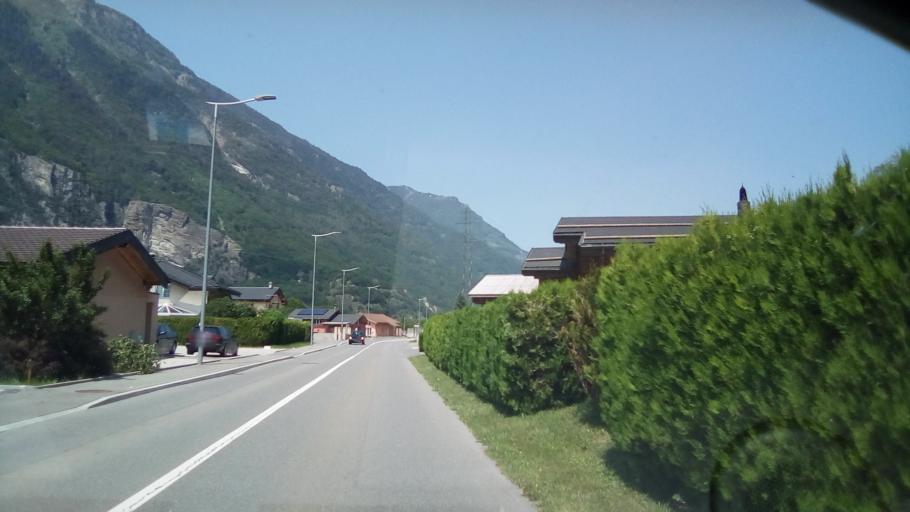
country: CH
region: Valais
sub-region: Saint-Maurice District
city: Vernayaz
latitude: 46.1452
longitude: 7.0437
